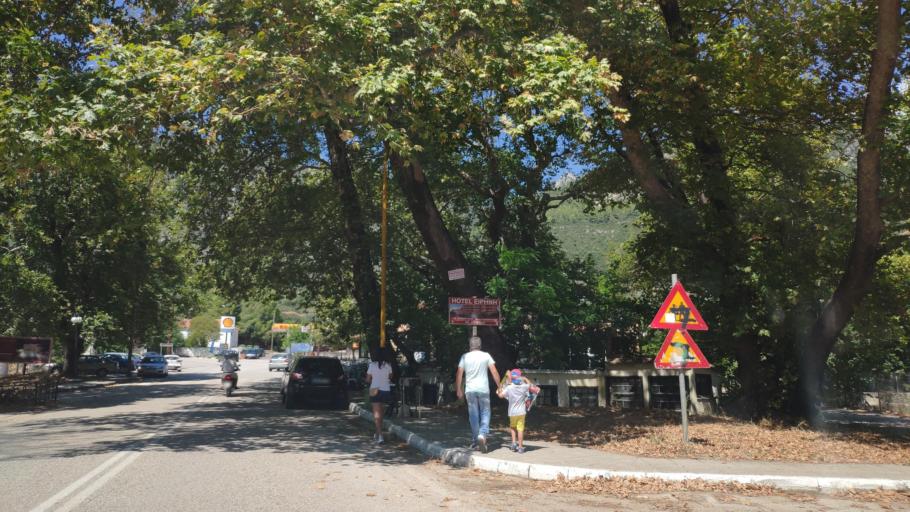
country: GR
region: Epirus
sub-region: Nomos Prevezis
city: Kanalaki
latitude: 39.3258
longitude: 20.6074
